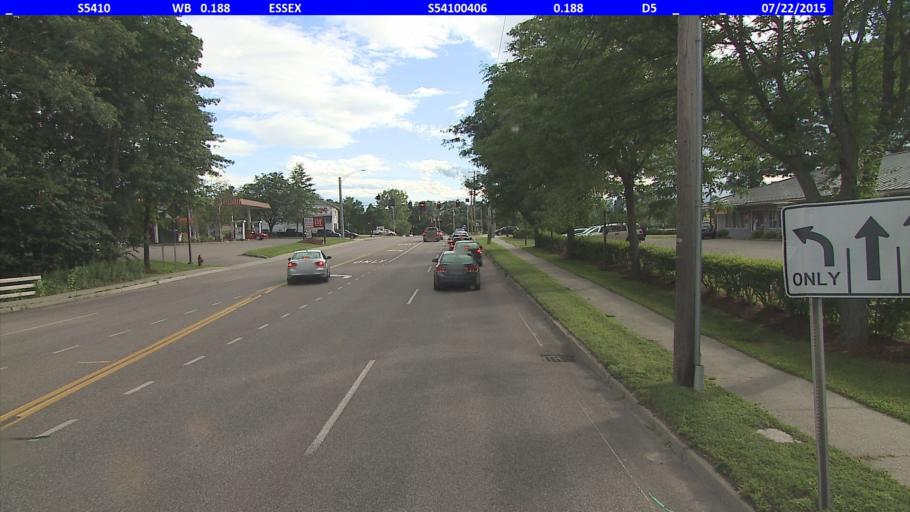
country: US
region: Vermont
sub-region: Chittenden County
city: Essex Junction
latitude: 44.5064
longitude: -73.1356
